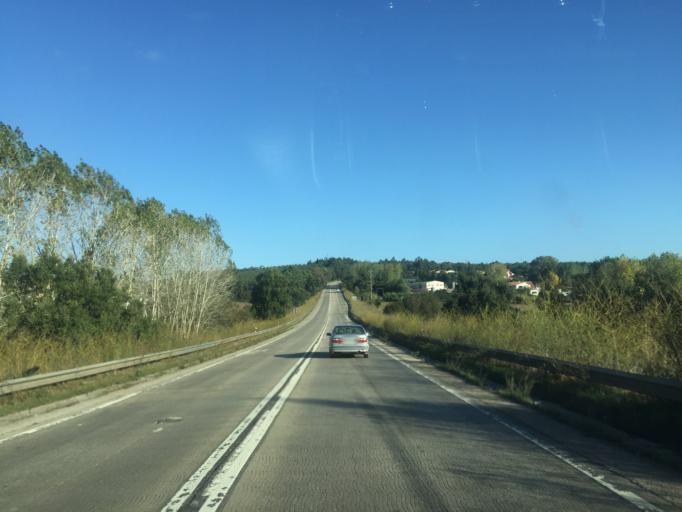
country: PT
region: Santarem
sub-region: Rio Maior
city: Rio Maior
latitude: 39.2948
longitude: -8.9479
